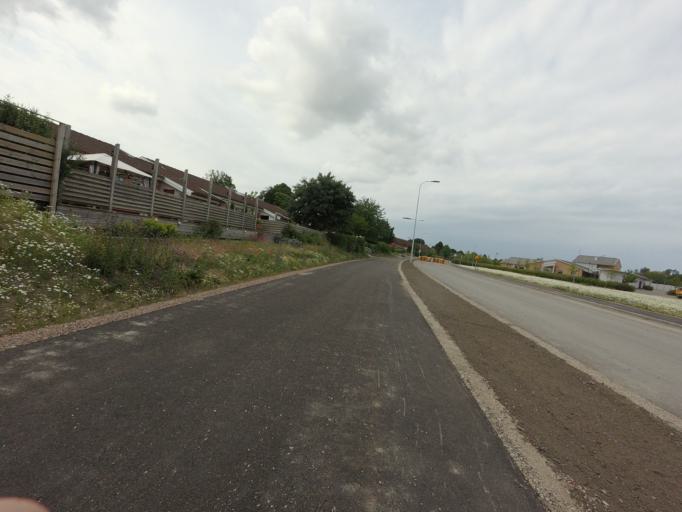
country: SE
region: Skane
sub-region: Staffanstorps Kommun
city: Hjaerup
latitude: 55.6558
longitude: 13.1204
